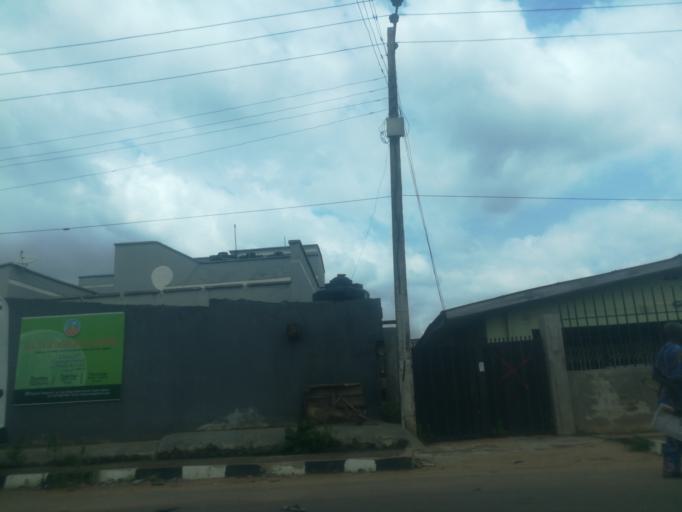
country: NG
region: Oyo
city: Ibadan
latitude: 7.3643
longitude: 3.8453
